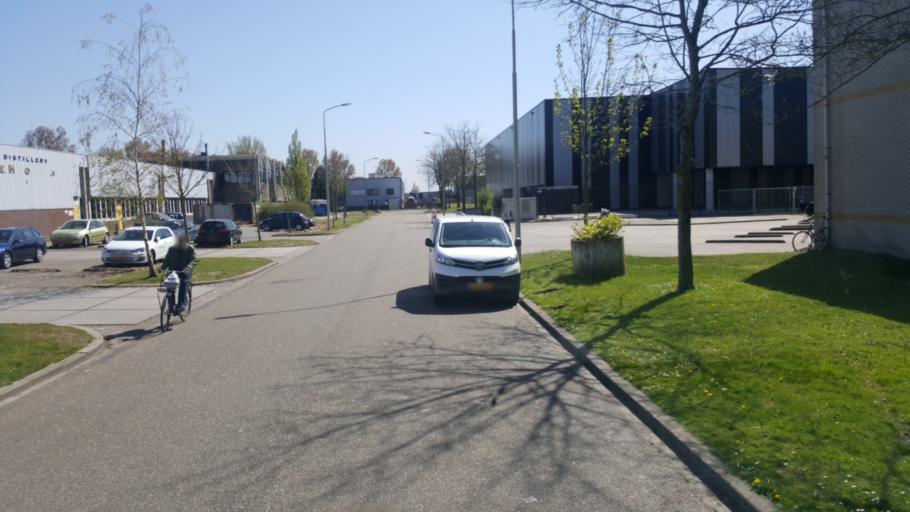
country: NL
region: North Holland
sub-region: Gemeente Hoorn
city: Hoorn
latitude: 52.6387
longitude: 5.1025
